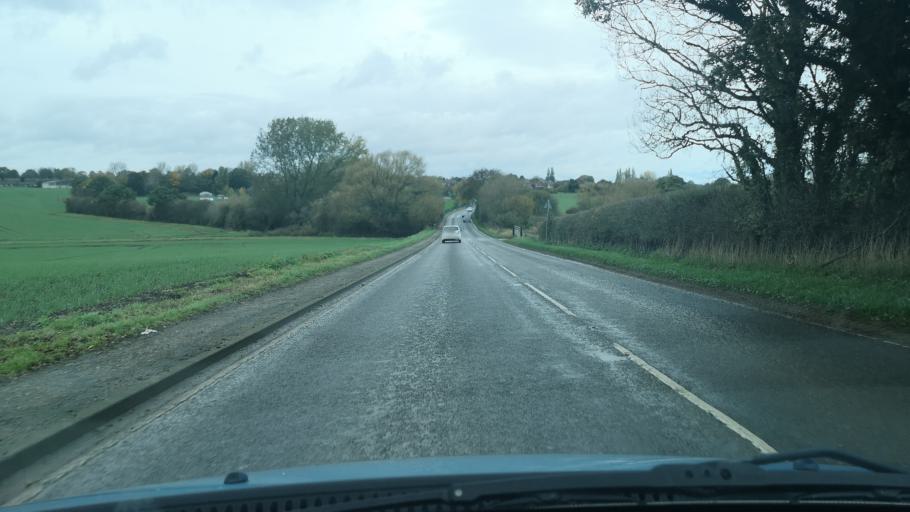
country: GB
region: England
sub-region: City and Borough of Wakefield
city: Low Ackworth
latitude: 53.6328
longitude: -1.3358
